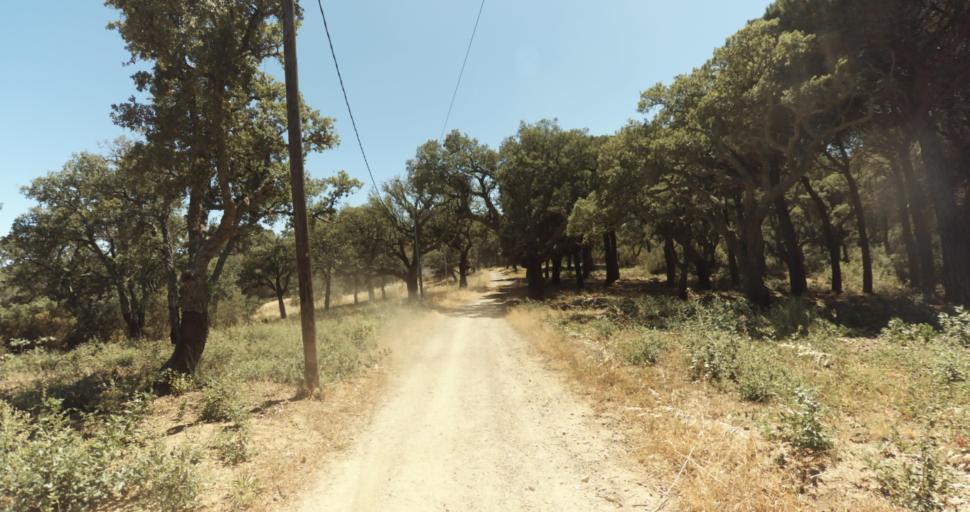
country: FR
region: Provence-Alpes-Cote d'Azur
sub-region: Departement du Var
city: Gassin
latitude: 43.2539
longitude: 6.5650
